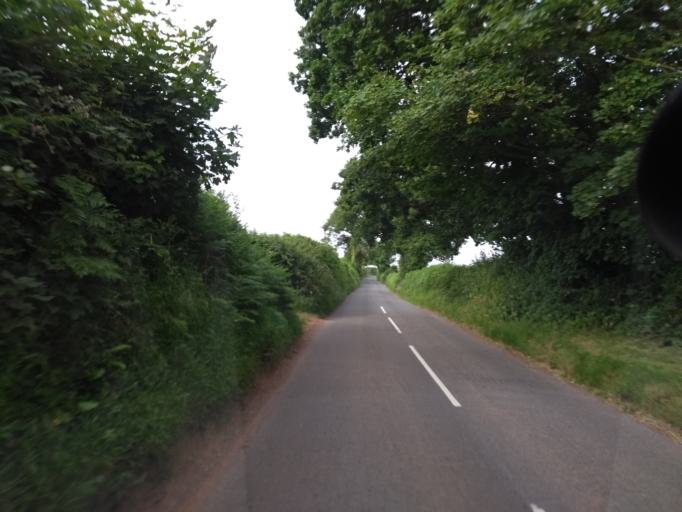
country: GB
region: England
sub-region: Somerset
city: Williton
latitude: 51.1540
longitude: -3.3483
